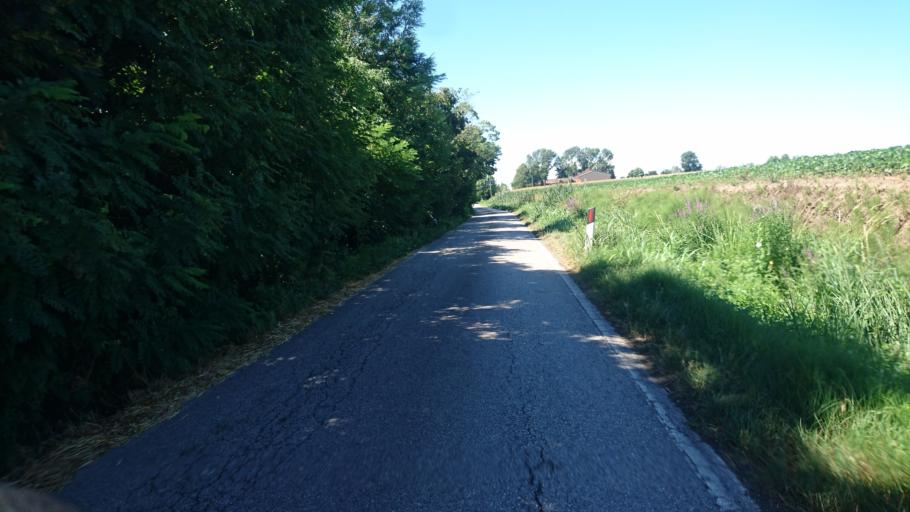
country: IT
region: Veneto
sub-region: Provincia di Padova
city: Campagnola
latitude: 45.2711
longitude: 12.0181
